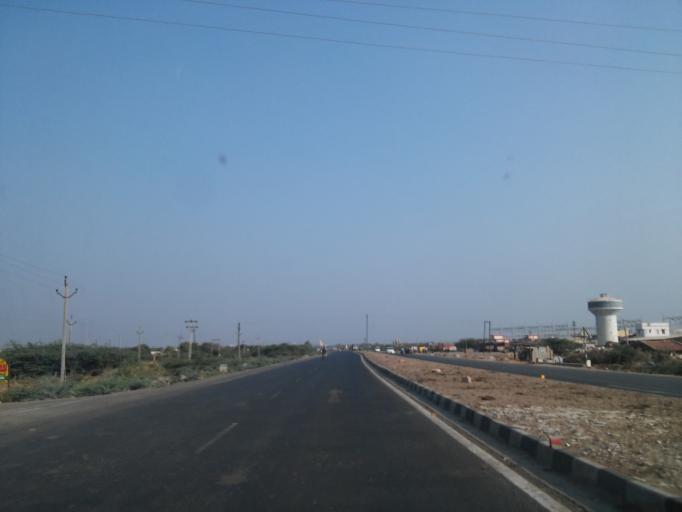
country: IN
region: Gujarat
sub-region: Surendranagar
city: Halvad
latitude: 23.0149
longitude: 71.2077
